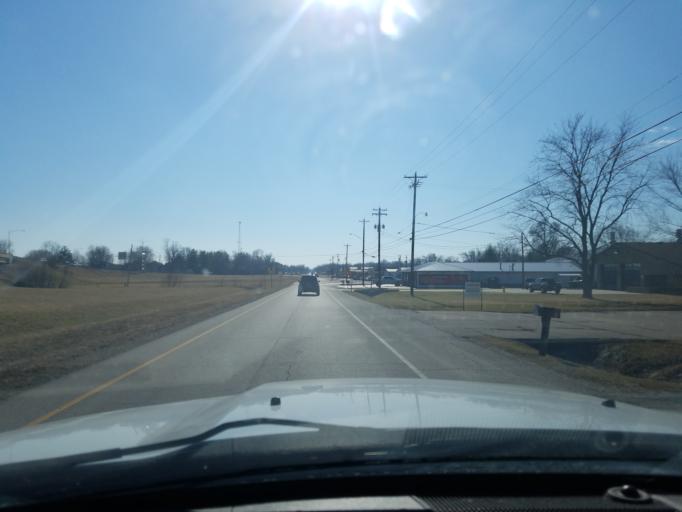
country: US
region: Kentucky
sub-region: Henderson County
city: Henderson
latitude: 37.8256
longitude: -87.5679
